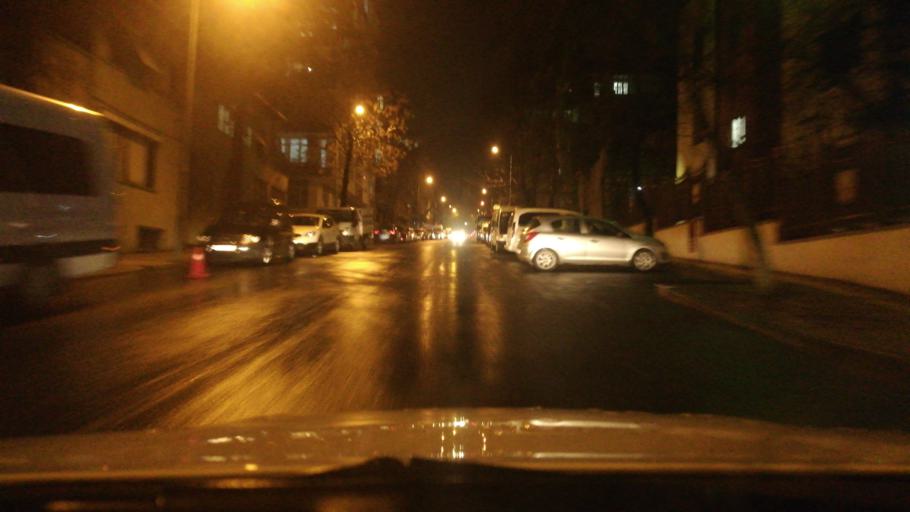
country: TR
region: Kahramanmaras
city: Kahramanmaras
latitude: 37.5905
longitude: 36.9291
